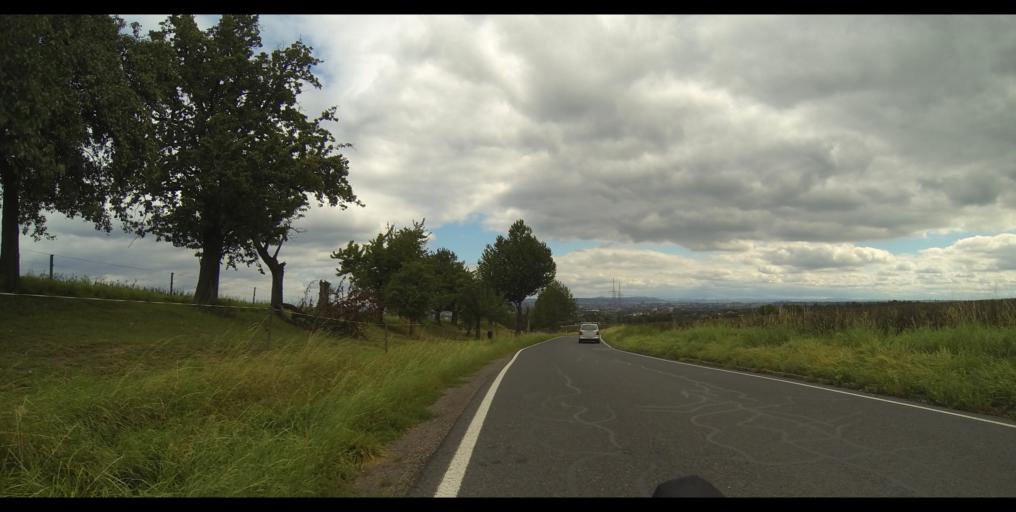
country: DE
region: Saxony
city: Radebeul
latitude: 51.0689
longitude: 13.6424
